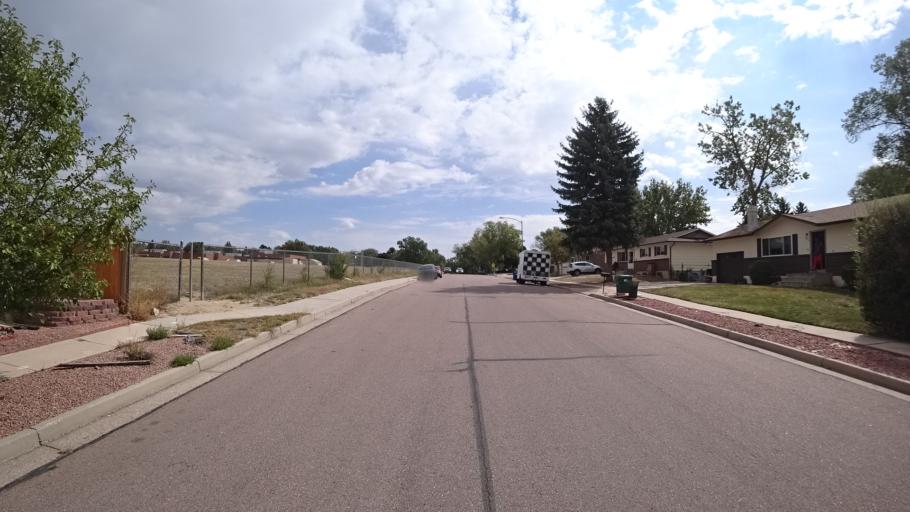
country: US
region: Colorado
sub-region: El Paso County
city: Cimarron Hills
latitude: 38.8506
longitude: -104.7352
